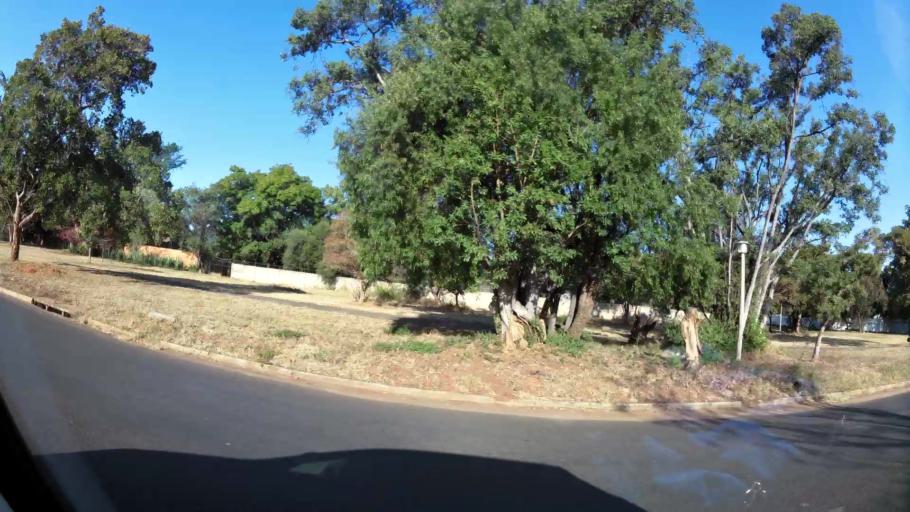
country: ZA
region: North-West
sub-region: Bojanala Platinum District Municipality
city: Rustenburg
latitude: -25.6866
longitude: 27.2389
